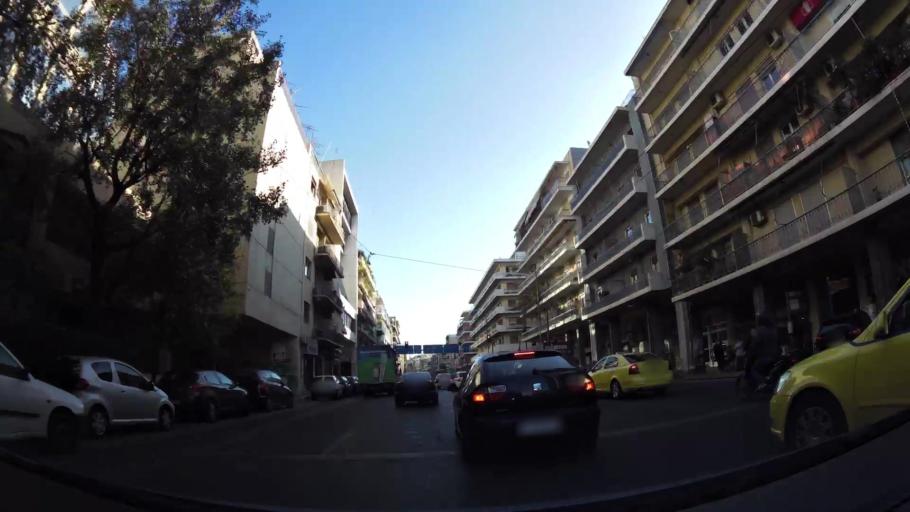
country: GR
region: Attica
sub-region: Nomarchia Athinas
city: Kaisariani
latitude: 37.9848
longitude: 23.7617
